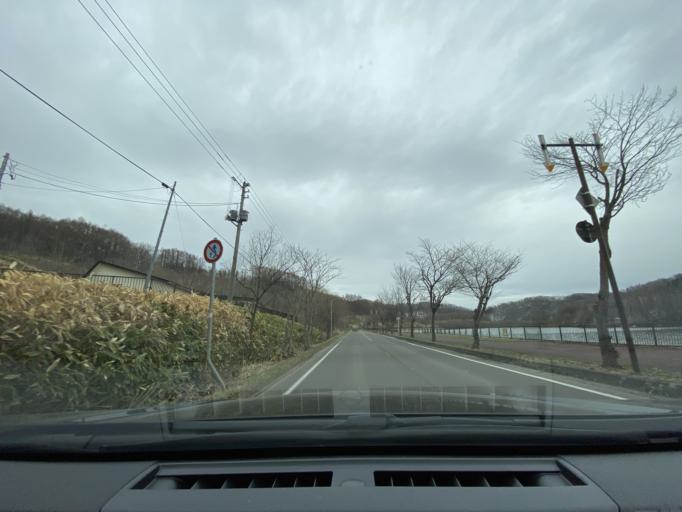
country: JP
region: Hokkaido
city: Nayoro
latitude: 44.0974
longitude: 142.4335
